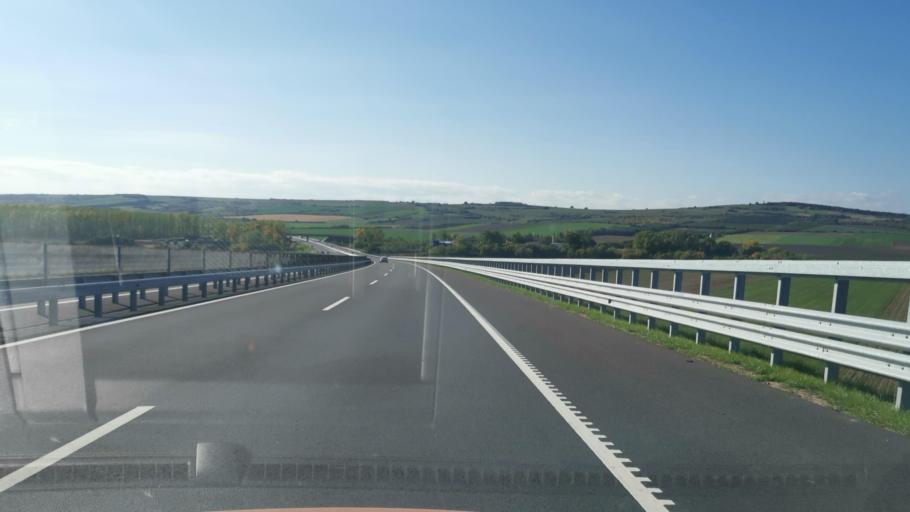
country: HU
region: Borsod-Abauj-Zemplen
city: Szikszo
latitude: 48.2127
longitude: 20.9214
